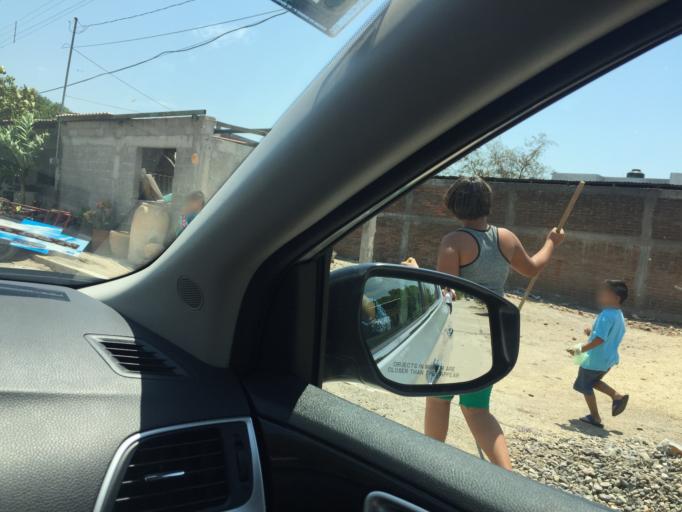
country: MX
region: Oaxaca
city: Asuncion Ixtaltepec
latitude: 16.5068
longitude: -95.0649
